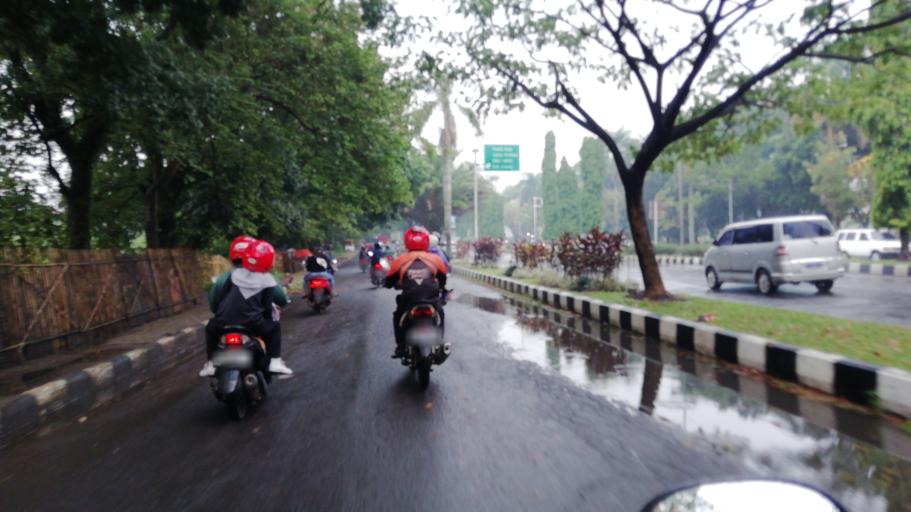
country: ID
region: West Java
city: Cibinong
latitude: -6.4820
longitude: 106.8208
